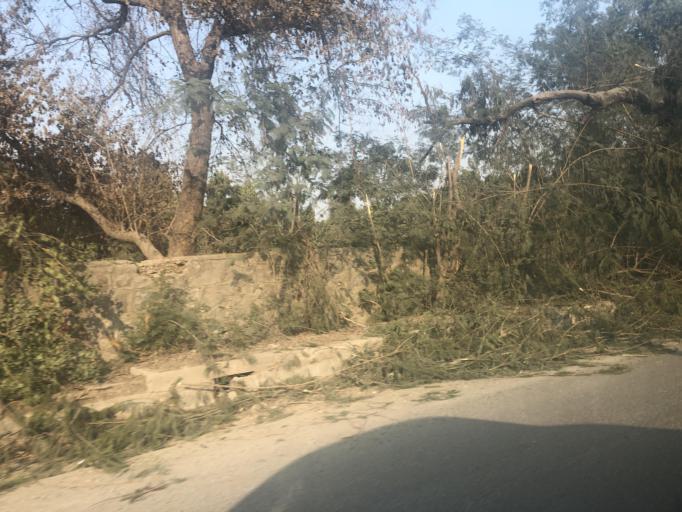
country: IN
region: Haryana
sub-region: Gurgaon
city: Gurgaon
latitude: 28.5403
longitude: 77.0261
